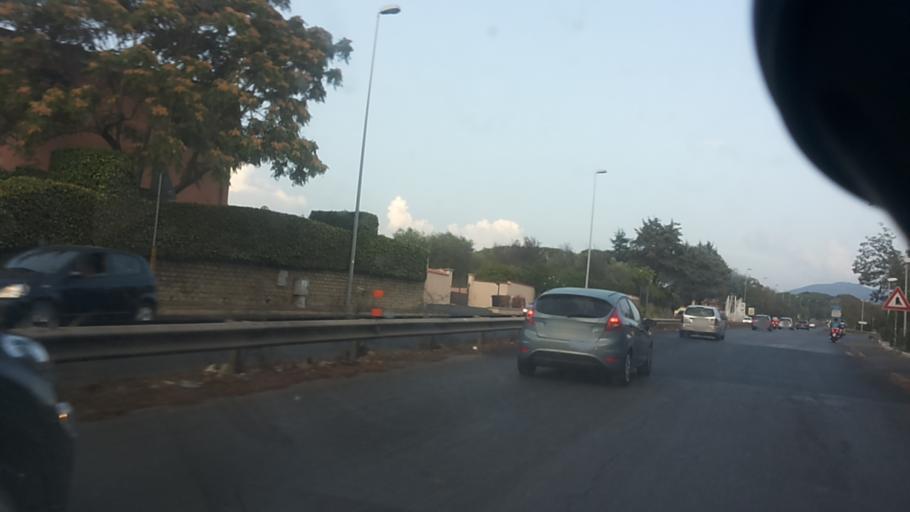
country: IT
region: Latium
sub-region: Citta metropolitana di Roma Capitale
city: Frascati
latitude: 41.8233
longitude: 12.6362
